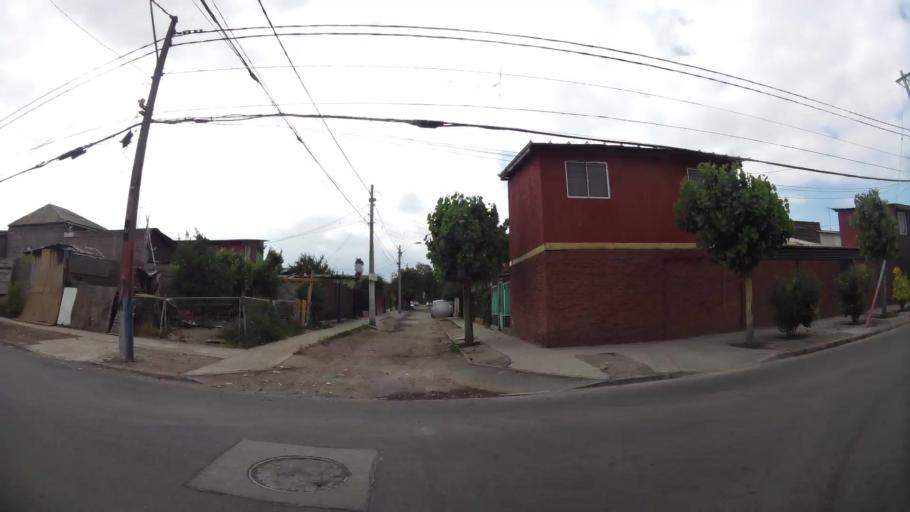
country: CL
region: Santiago Metropolitan
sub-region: Provincia de Maipo
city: San Bernardo
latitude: -33.5209
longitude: -70.6941
